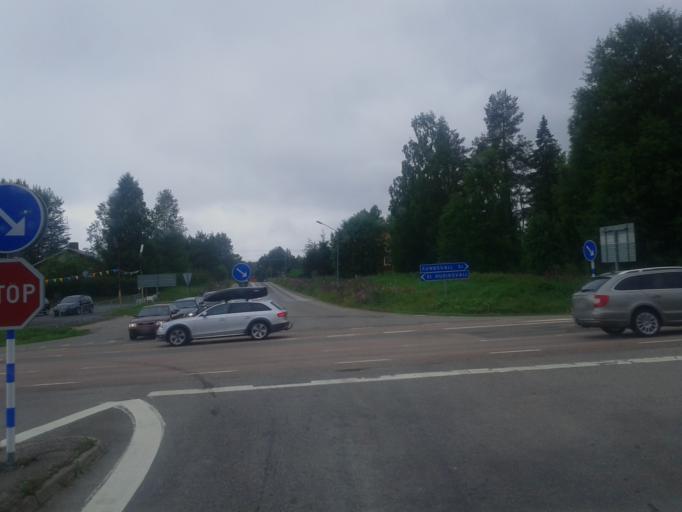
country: SE
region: Gaevleborg
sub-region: Nordanstigs Kommun
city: Bergsjoe
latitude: 61.9773
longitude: 17.2422
